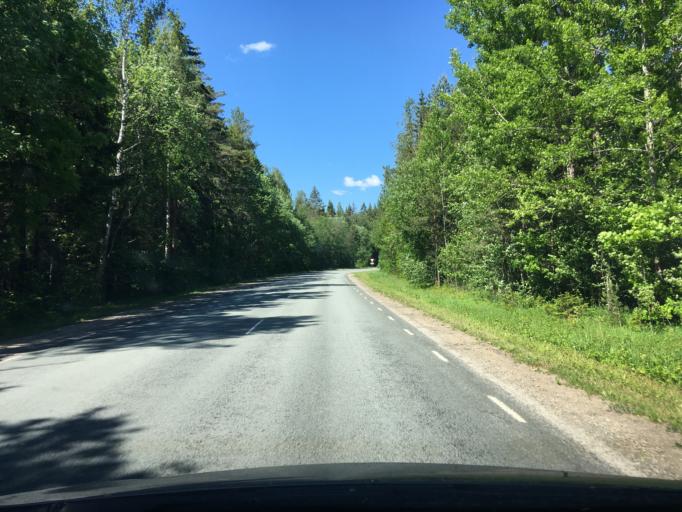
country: EE
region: Harju
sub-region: Rae vald
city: Vaida
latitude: 59.2052
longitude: 24.9449
